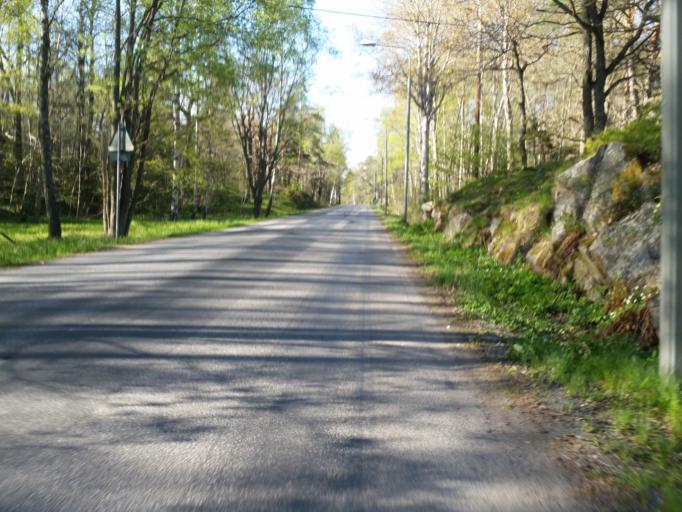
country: SE
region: Stockholm
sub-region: Nacka Kommun
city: Alta
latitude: 59.2526
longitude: 18.1362
